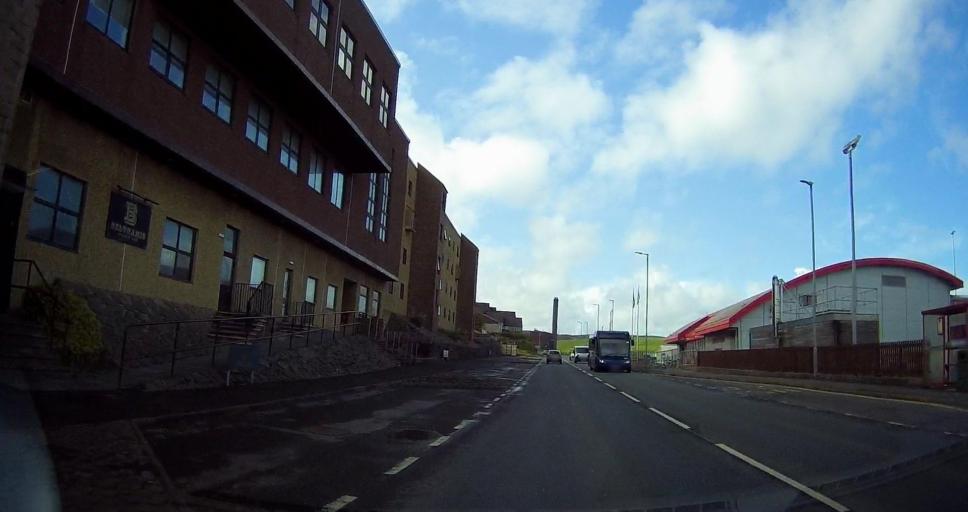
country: GB
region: Scotland
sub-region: Shetland Islands
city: Lerwick
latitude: 60.1616
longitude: -1.1584
